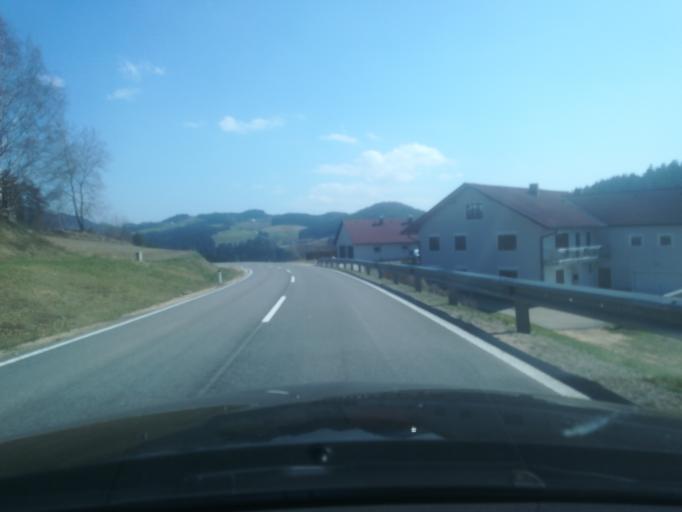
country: AT
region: Upper Austria
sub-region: Politischer Bezirk Perg
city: Sankt Georgen am Walde
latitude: 48.4173
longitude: 14.7596
